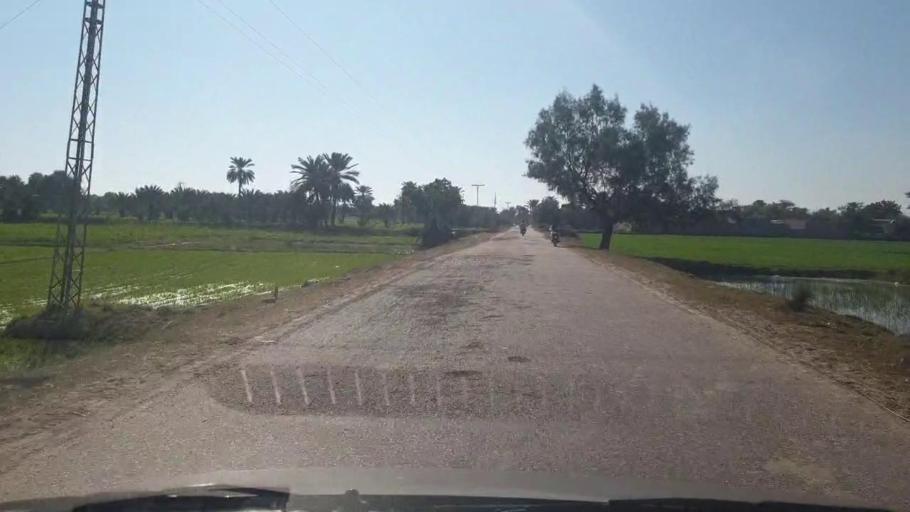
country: PK
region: Sindh
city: Bozdar
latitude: 27.1089
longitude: 68.6335
